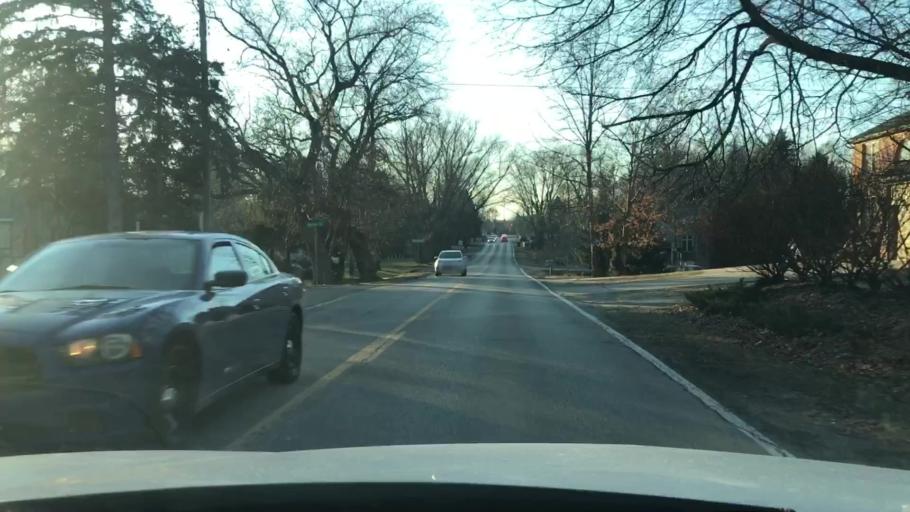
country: US
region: Michigan
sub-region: Oakland County
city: Wolverine Lake
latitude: 42.5989
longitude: -83.4416
